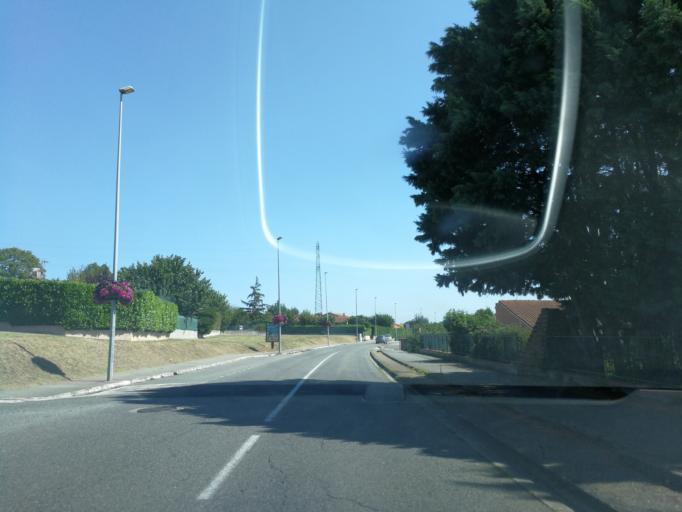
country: FR
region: Midi-Pyrenees
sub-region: Departement de la Haute-Garonne
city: Saint-Orens-de-Gameville
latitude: 43.5840
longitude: 1.5326
